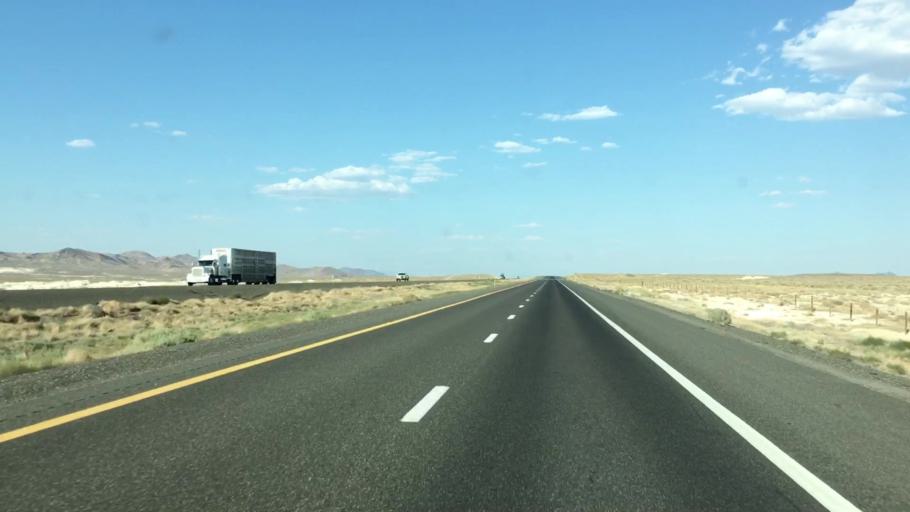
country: US
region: Nevada
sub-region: Lyon County
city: Fernley
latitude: 39.8332
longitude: -118.9659
